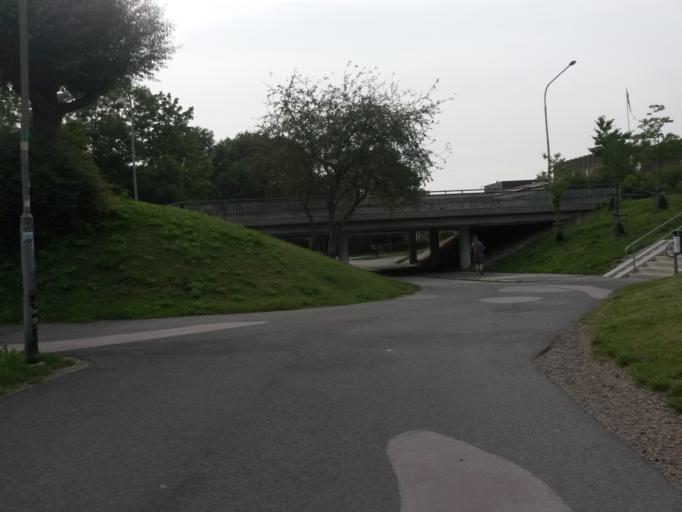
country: SE
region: Skane
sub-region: Lunds Kommun
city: Lund
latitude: 55.7228
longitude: 13.2029
